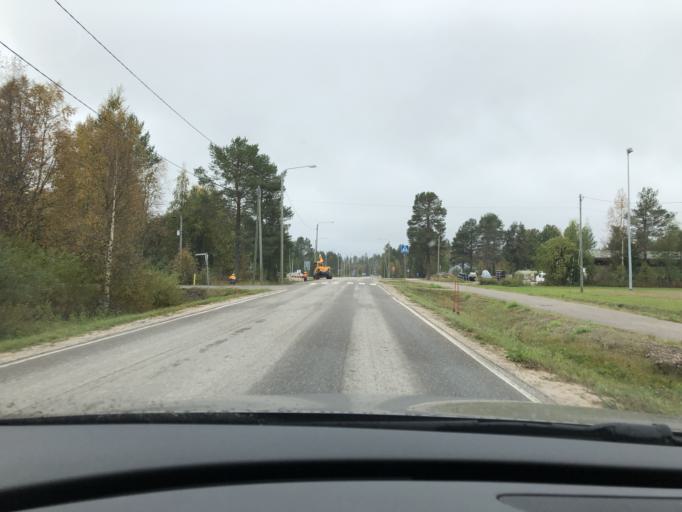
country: FI
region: Lapland
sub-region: Itae-Lappi
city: Posio
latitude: 66.1103
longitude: 28.1781
